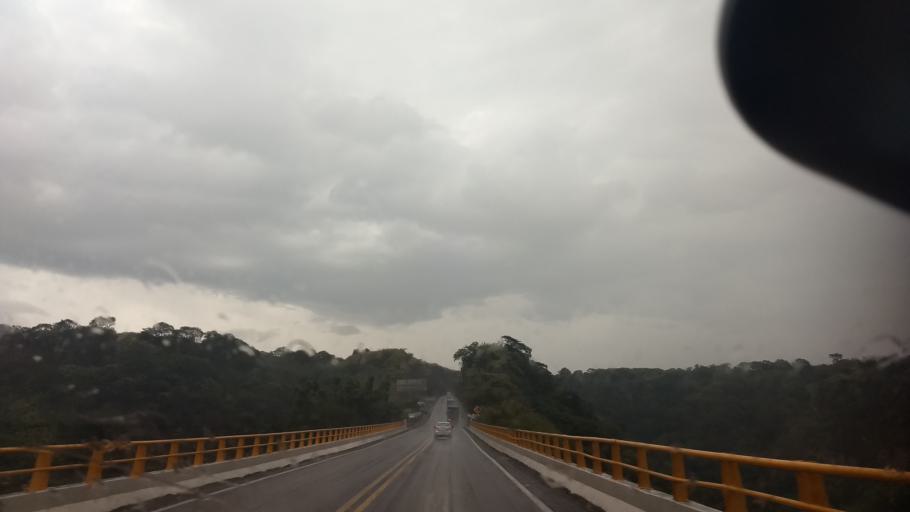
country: MX
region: Jalisco
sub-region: Tonila
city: San Marcos
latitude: 19.4441
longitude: -103.4748
